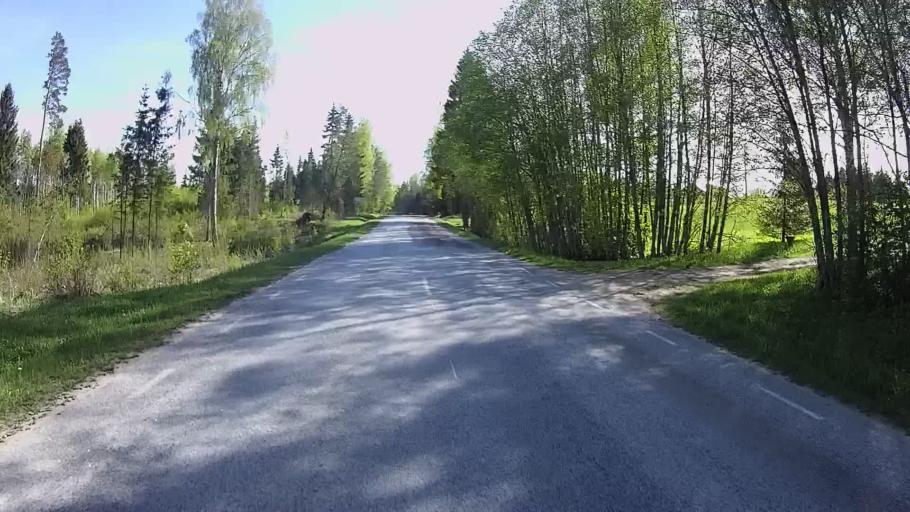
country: EE
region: Vorumaa
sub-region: Antsla vald
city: Vana-Antsla
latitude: 57.9998
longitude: 26.4970
